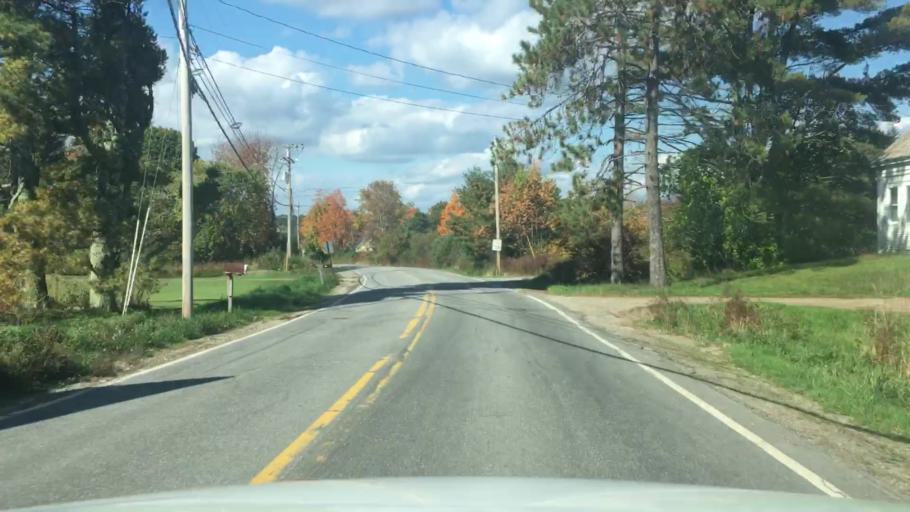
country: US
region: Maine
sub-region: Knox County
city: Warren
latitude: 44.1188
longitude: -69.2330
